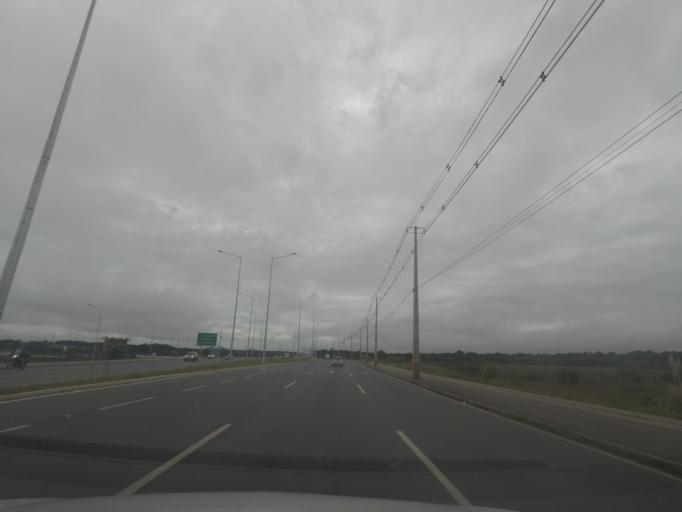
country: BR
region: Parana
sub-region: Pinhais
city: Pinhais
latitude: -25.4425
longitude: -49.1491
